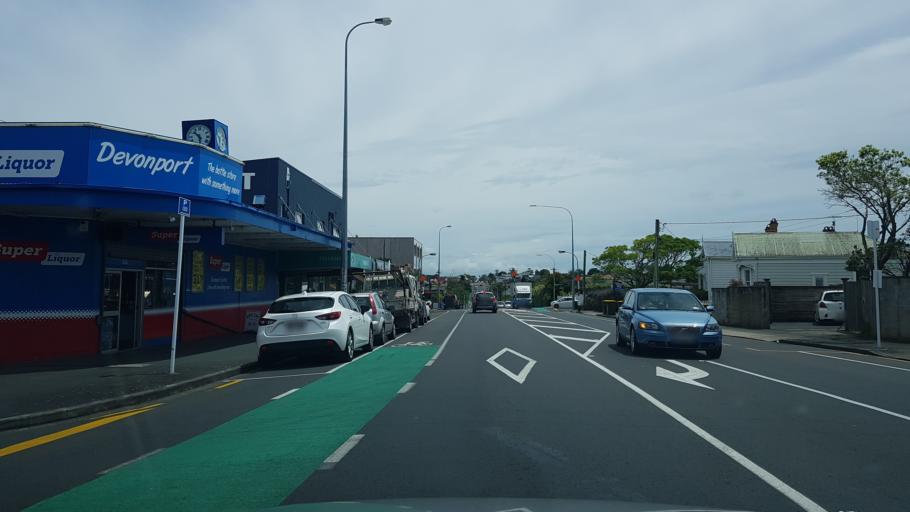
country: NZ
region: Auckland
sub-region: Auckland
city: North Shore
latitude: -36.8136
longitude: 174.7926
